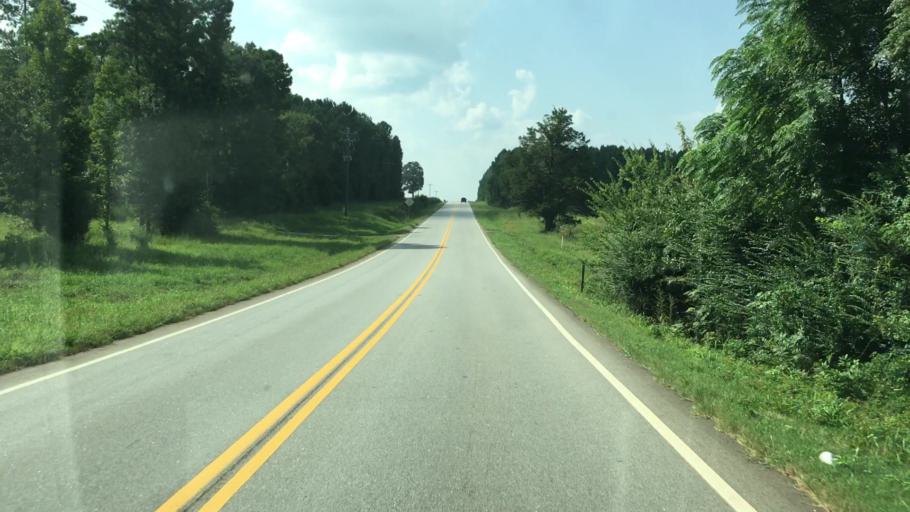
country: US
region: Georgia
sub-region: Jasper County
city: Monticello
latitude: 33.3845
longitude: -83.7462
